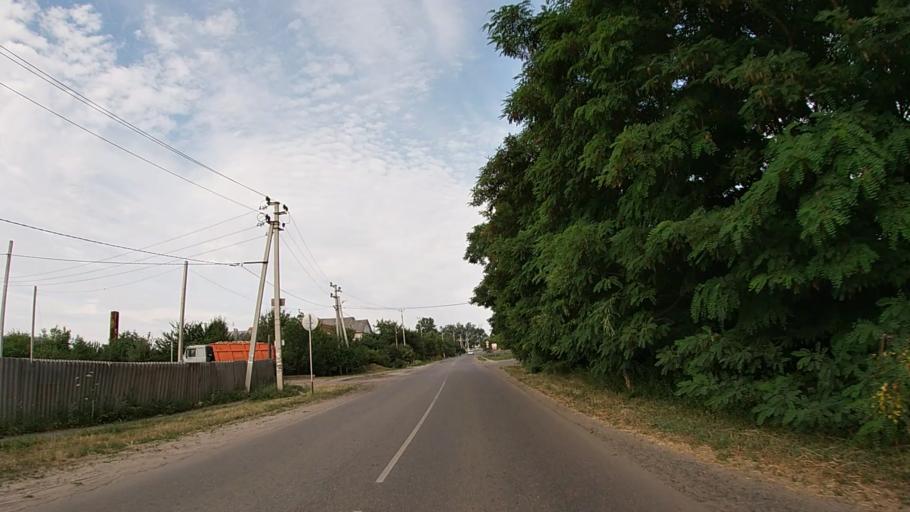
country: RU
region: Belgorod
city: Severnyy
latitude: 50.6911
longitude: 36.5618
